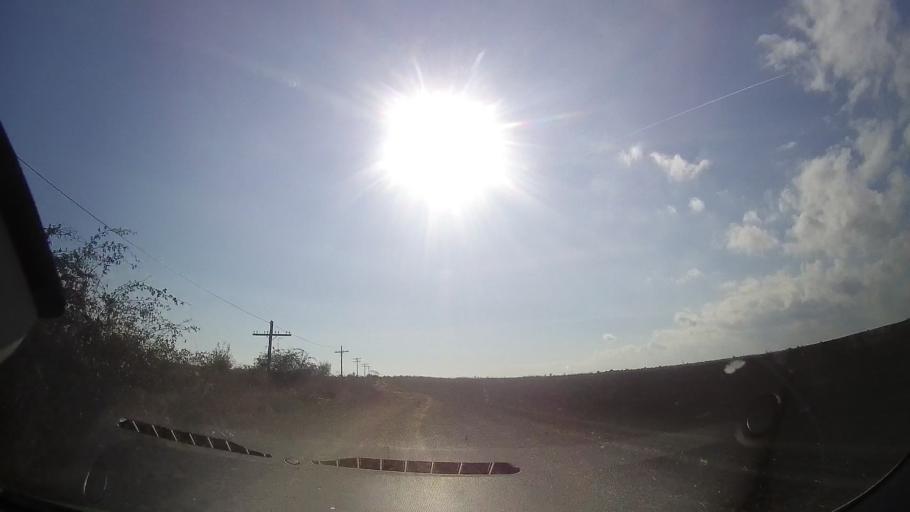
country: RO
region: Constanta
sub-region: Comuna Tuzla
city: Tuzla
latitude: 43.9808
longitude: 28.6444
